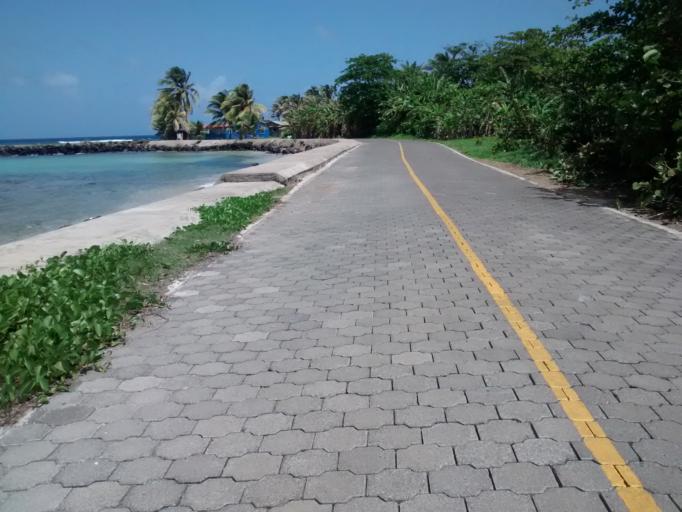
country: NI
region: Atlantico Sur
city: Corn Island
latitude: 12.1818
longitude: -83.0626
